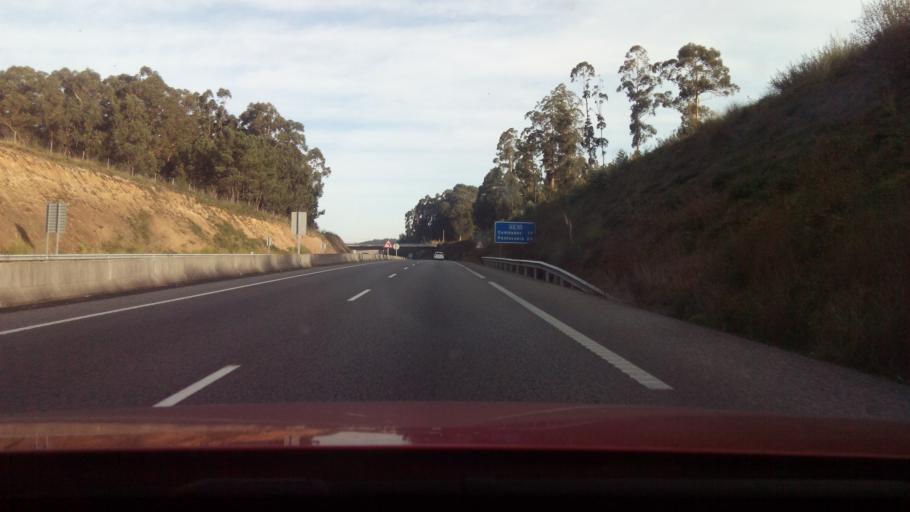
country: ES
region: Galicia
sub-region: Provincia de Pontevedra
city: Sanxenxo
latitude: 42.4189
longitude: -8.8086
